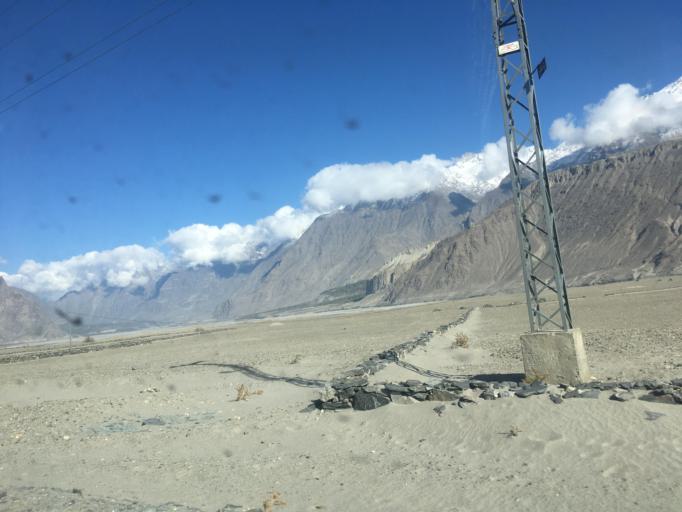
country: PK
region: Gilgit-Baltistan
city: Skardu
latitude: 35.3587
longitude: 75.5367
